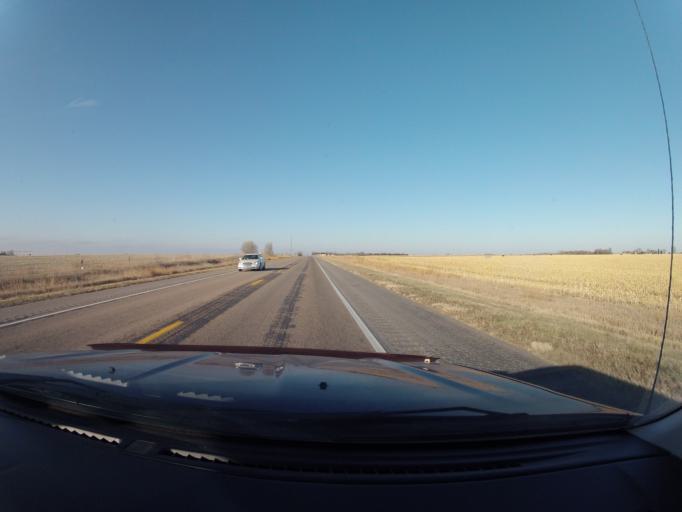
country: US
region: Nebraska
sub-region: Kearney County
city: Minden
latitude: 40.5644
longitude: -98.9518
